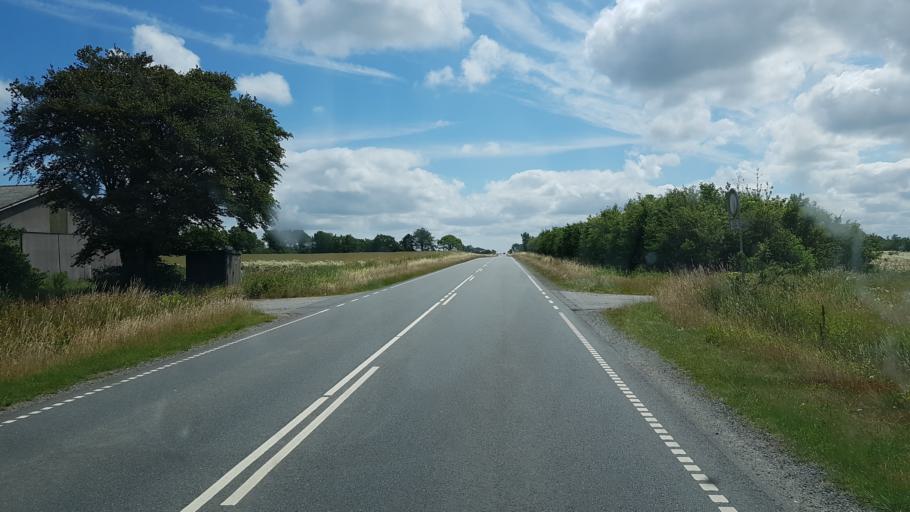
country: DK
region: South Denmark
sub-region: Vejen Kommune
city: Rodding
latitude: 55.3760
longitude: 9.0642
